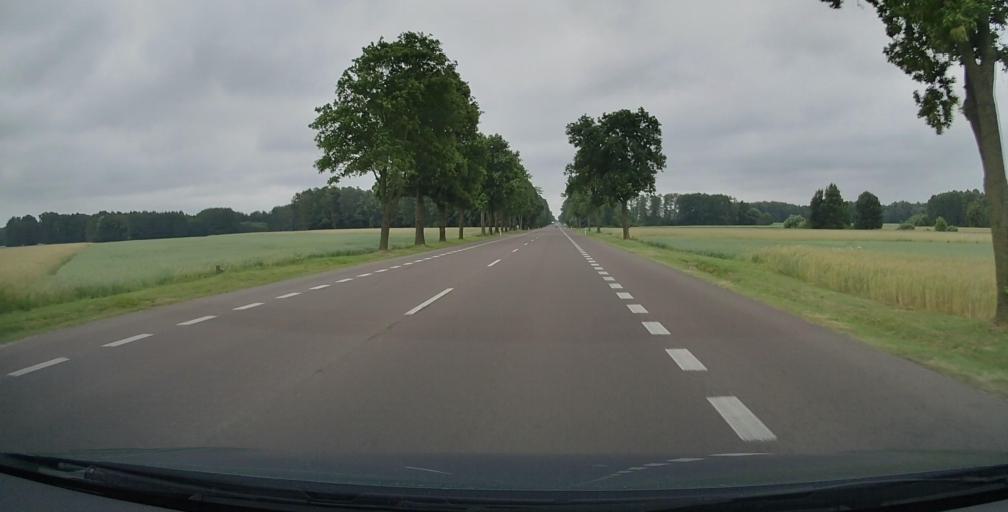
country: PL
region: Lublin Voivodeship
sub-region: Powiat bialski
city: Rzeczyca
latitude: 52.0462
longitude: 22.6786
